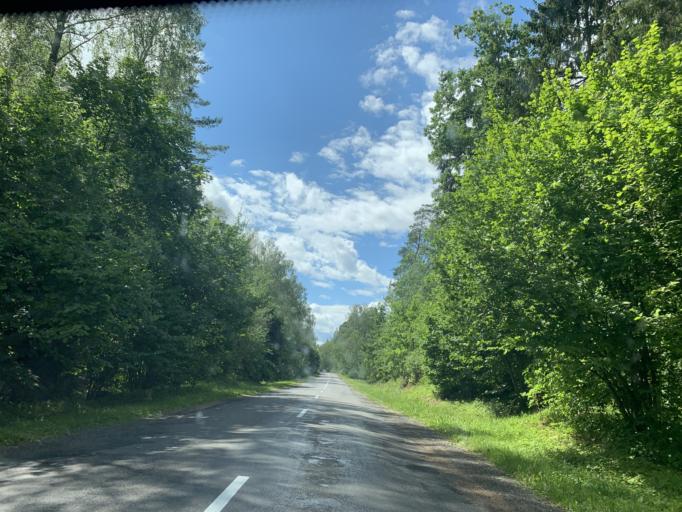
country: BY
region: Minsk
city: Rakaw
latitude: 53.9860
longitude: 26.9680
